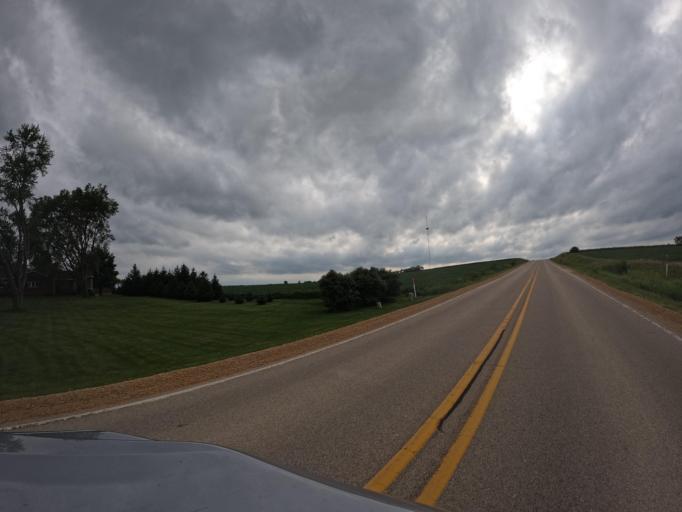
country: US
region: Iowa
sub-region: Clinton County
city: De Witt
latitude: 41.8005
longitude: -90.5275
